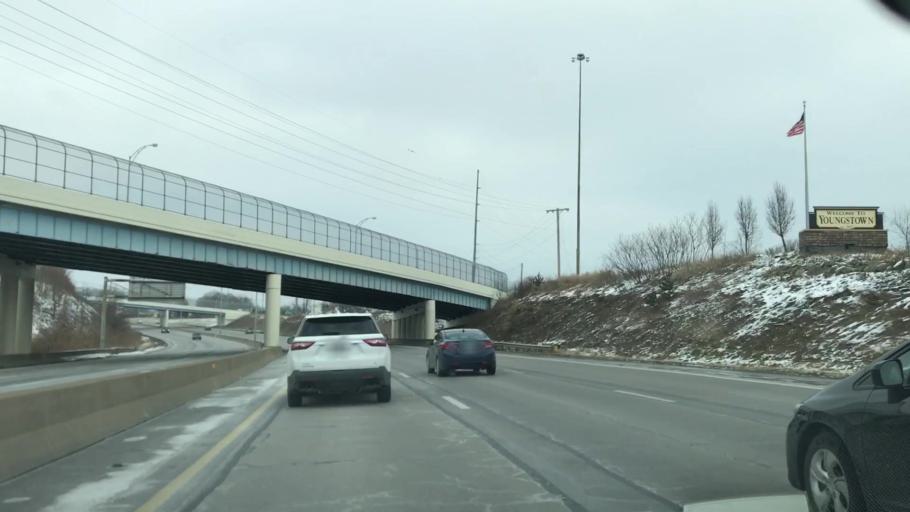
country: US
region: Ohio
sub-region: Mahoning County
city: Campbell
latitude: 41.0729
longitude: -80.6255
